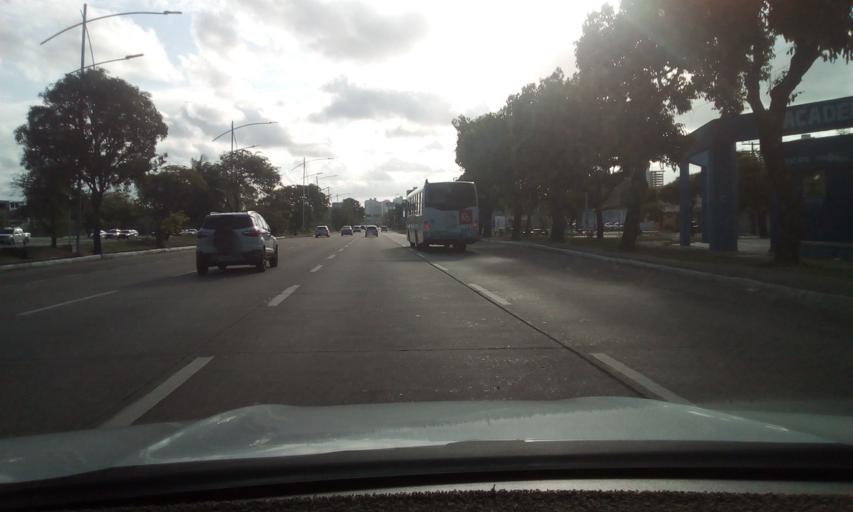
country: BR
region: Pernambuco
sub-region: Recife
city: Recife
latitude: -8.0380
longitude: -34.8756
